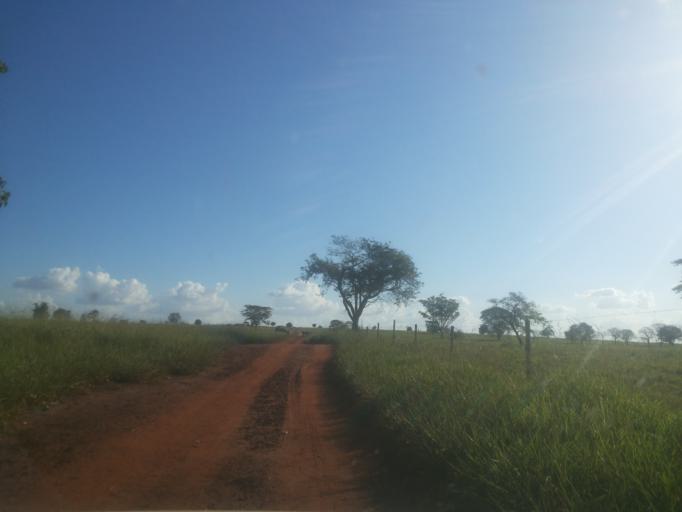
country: BR
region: Minas Gerais
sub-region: Santa Vitoria
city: Santa Vitoria
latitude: -18.9998
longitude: -50.4524
